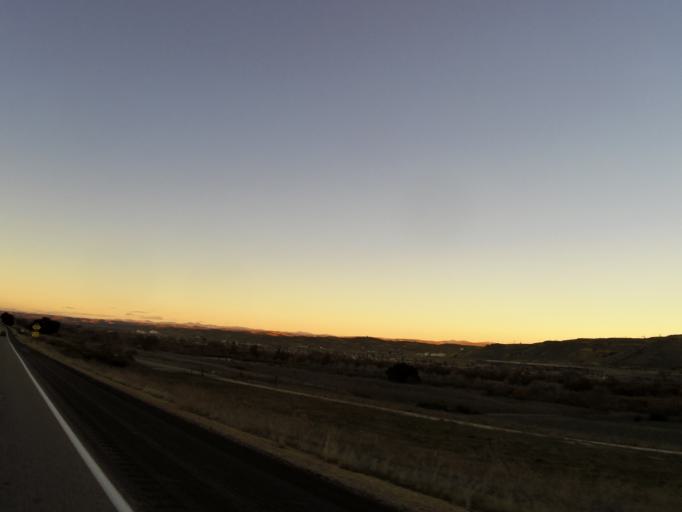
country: US
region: California
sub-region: San Luis Obispo County
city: Lake Nacimiento
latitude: 35.9359
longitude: -120.8721
